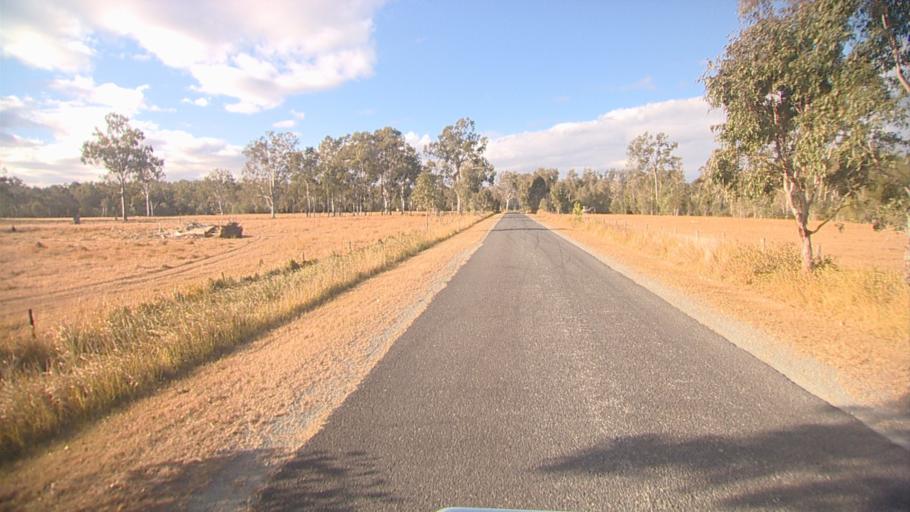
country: AU
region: Queensland
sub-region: Logan
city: Cedar Vale
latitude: -27.8868
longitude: 153.0738
